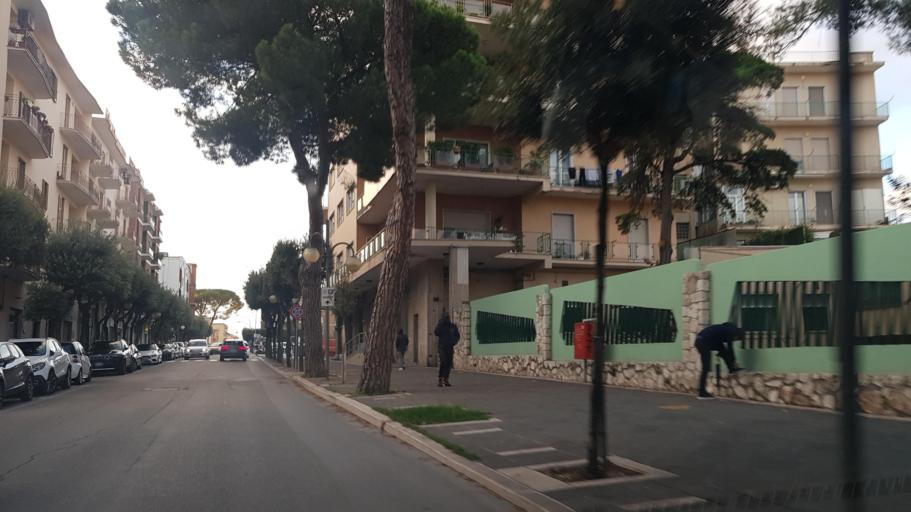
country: IT
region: Basilicate
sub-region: Provincia di Matera
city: Matera
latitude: 40.6719
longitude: 16.6039
